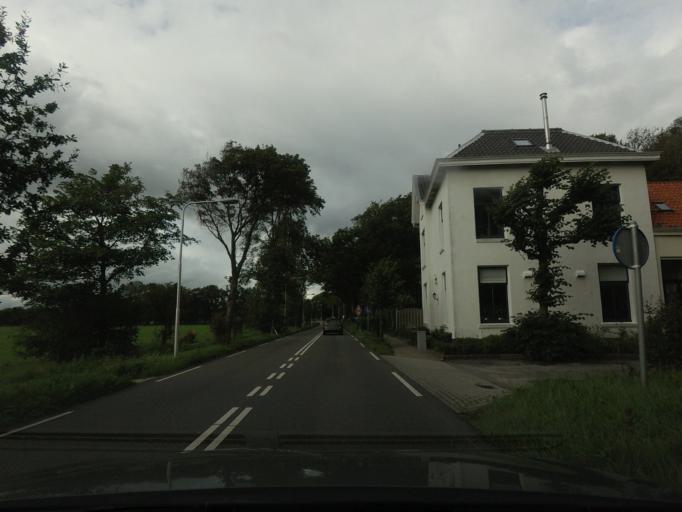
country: NL
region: North Holland
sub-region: Gemeente Bloemendaal
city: Bennebroek
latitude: 52.3242
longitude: 4.5784
